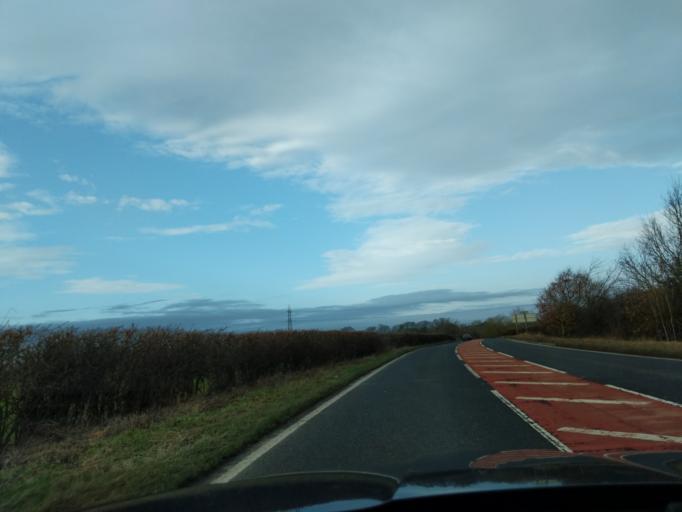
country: GB
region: England
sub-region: Northumberland
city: Darras Hall
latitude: 55.0558
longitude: -1.7652
